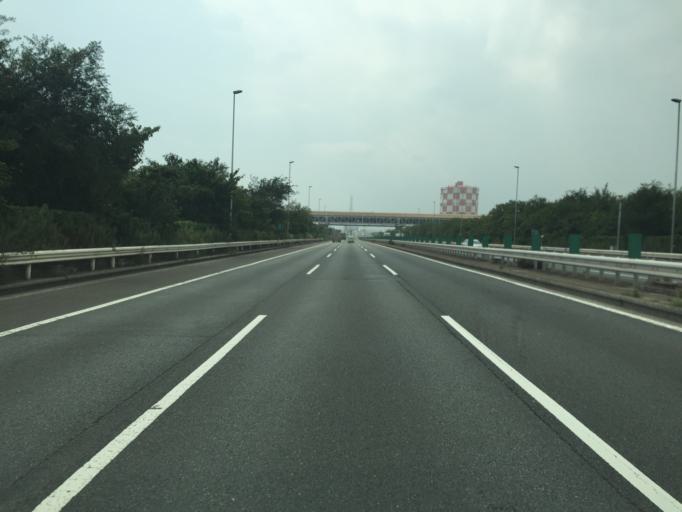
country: JP
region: Kanagawa
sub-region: Kawasaki-shi
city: Kawasaki
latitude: 35.4840
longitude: 139.7263
